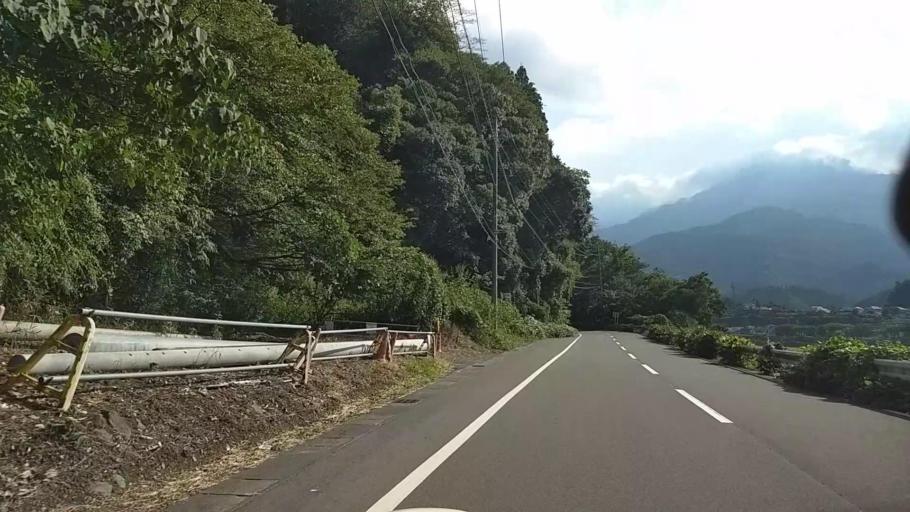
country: JP
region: Shizuoka
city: Fujinomiya
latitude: 35.2903
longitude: 138.4601
